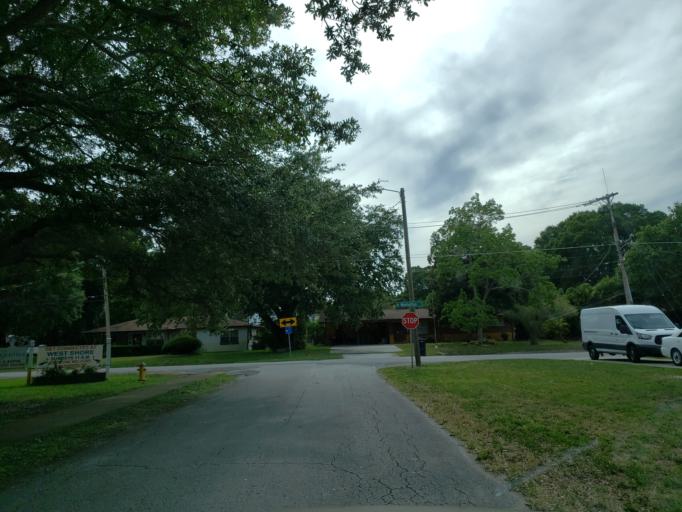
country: US
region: Florida
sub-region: Hillsborough County
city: Tampa
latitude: 27.9476
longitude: -82.5177
